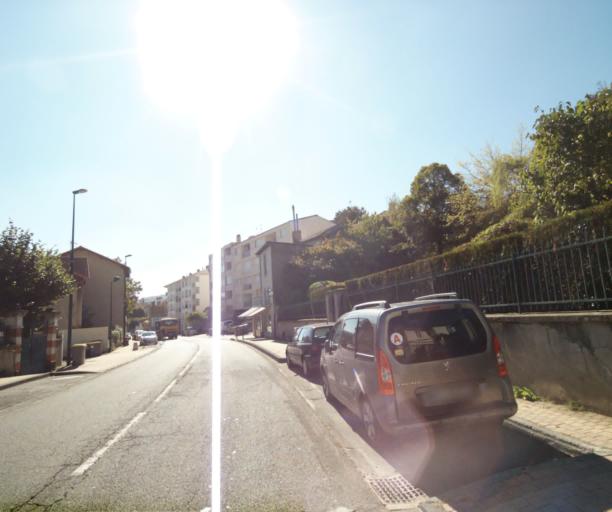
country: FR
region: Auvergne
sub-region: Departement du Puy-de-Dome
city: Chamalieres
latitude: 45.7831
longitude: 3.0630
